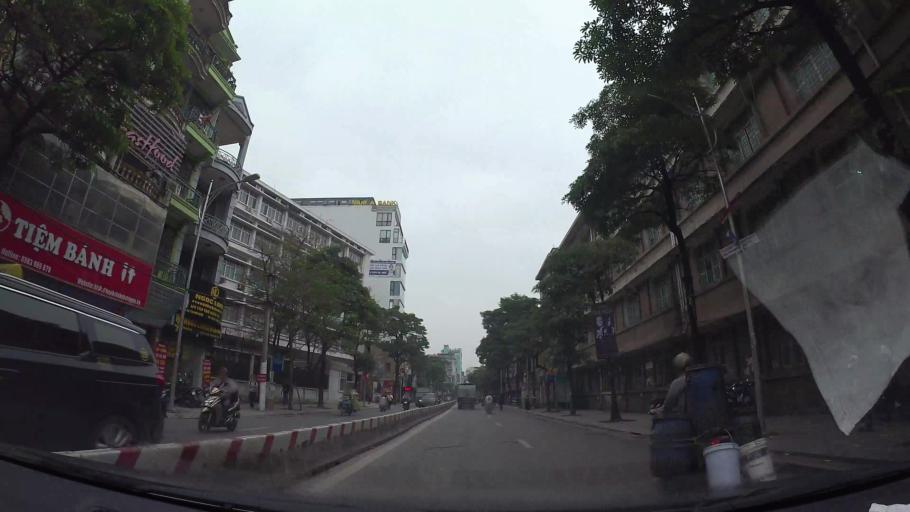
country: VN
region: Ha Noi
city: Hai BaTrung
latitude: 21.0035
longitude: 105.8487
